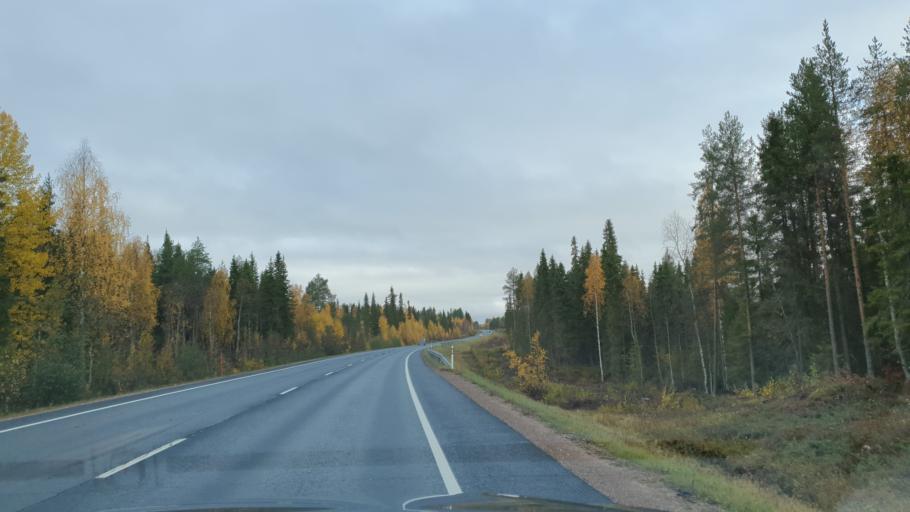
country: FI
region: Lapland
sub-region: Rovaniemi
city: Rovaniemi
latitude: 66.6155
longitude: 25.5497
